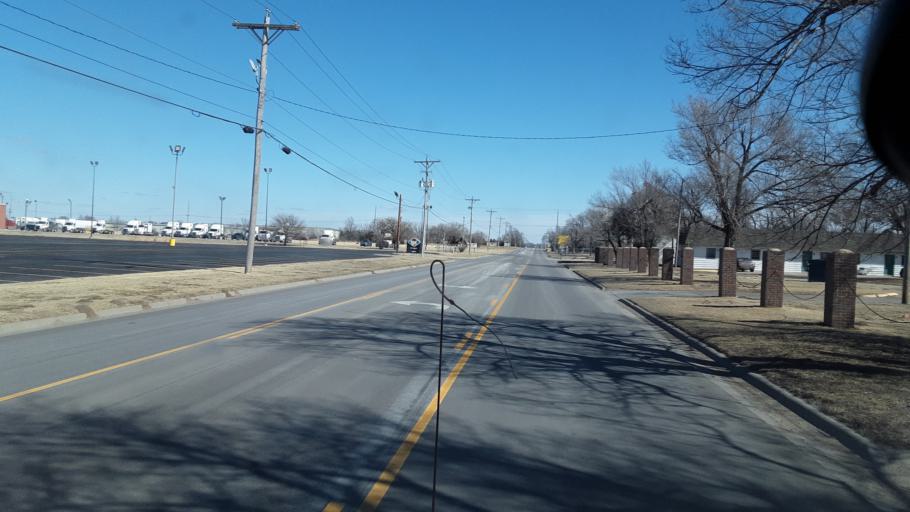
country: US
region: Kansas
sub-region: Reno County
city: Hutchinson
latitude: 38.0577
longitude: -97.8802
